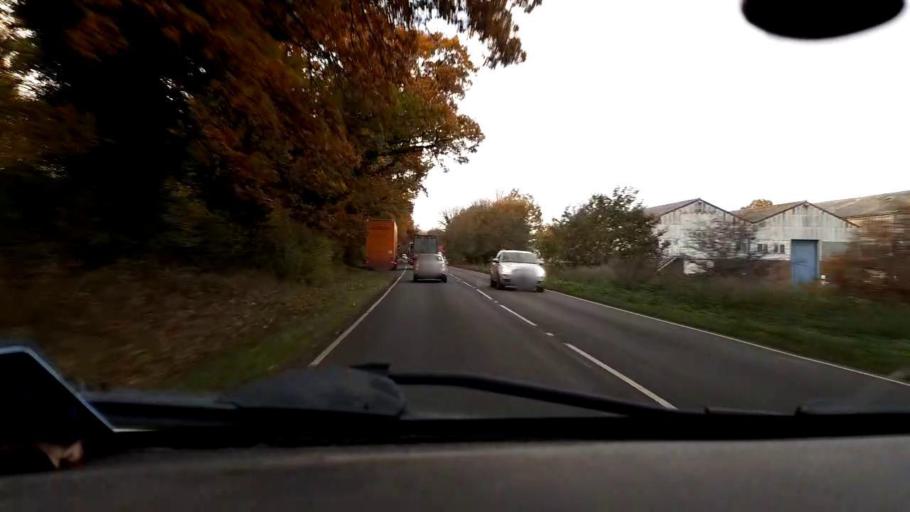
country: GB
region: England
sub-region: Norfolk
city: Costessey
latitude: 52.7165
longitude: 1.1285
